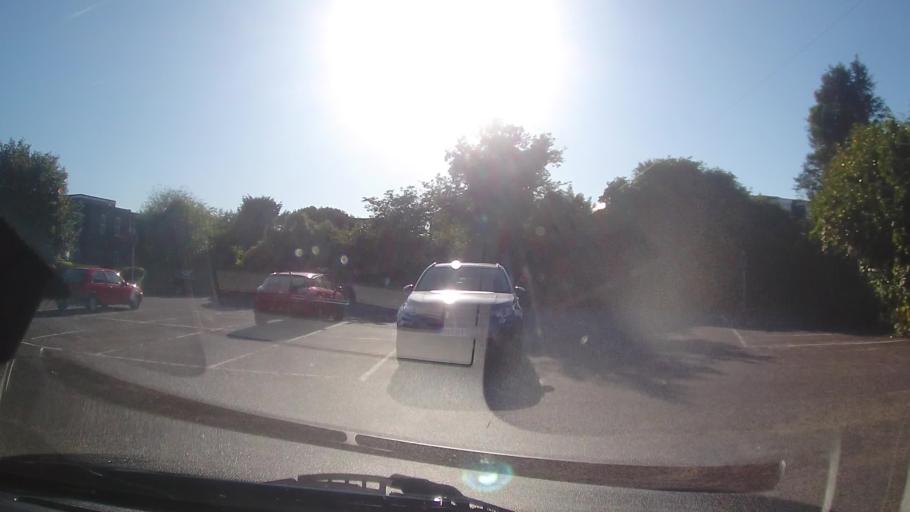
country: GB
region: England
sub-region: Buckinghamshire
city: Beaconsfield
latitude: 51.6031
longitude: -0.6367
